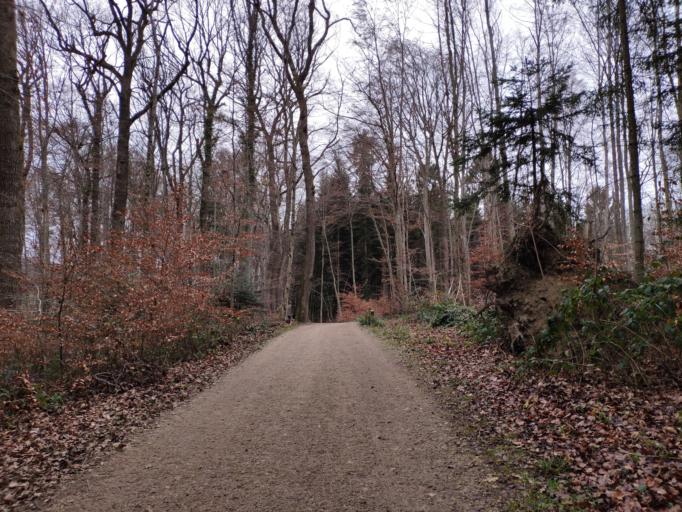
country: CH
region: Basel-City
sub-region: Basel-Stadt
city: Bettingen
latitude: 47.5677
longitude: 7.6776
